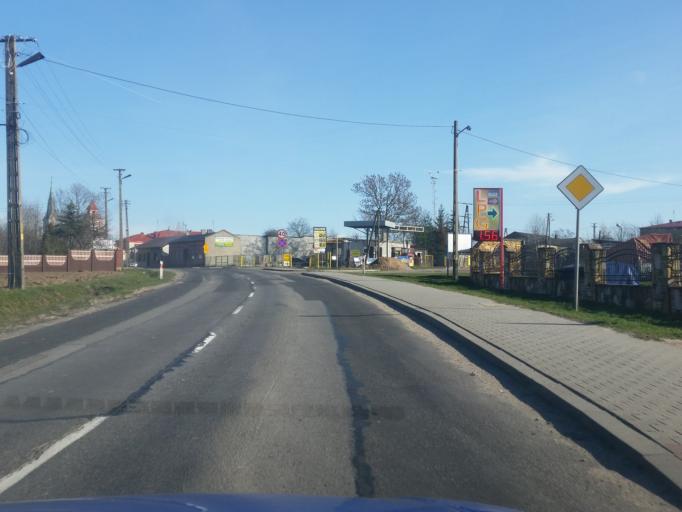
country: PL
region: Lodz Voivodeship
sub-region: Powiat radomszczanski
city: Kamiensk
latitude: 51.2059
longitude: 19.4939
